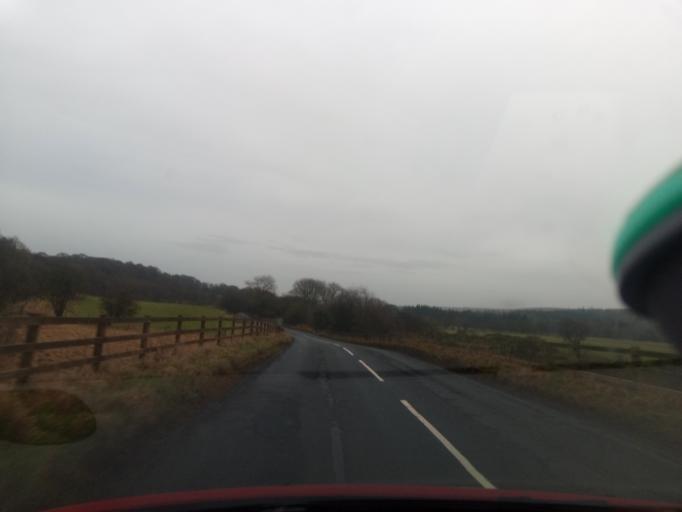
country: GB
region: England
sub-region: Northumberland
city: Rochester
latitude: 55.1568
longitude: -2.2976
